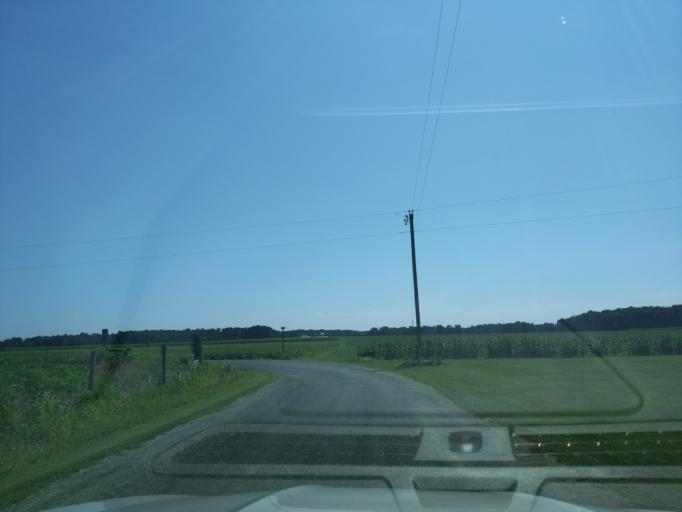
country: US
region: Indiana
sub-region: Ripley County
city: Osgood
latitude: 39.0885
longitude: -85.4331
